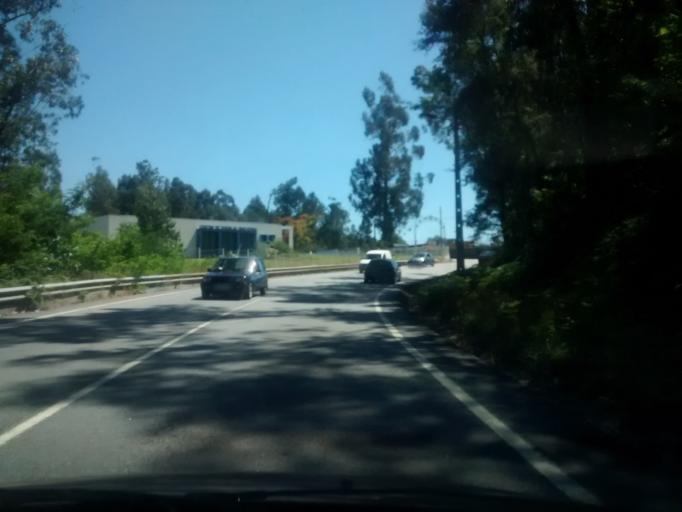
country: PT
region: Braga
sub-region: Barcelos
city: Galegos
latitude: 41.5308
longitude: -8.5563
